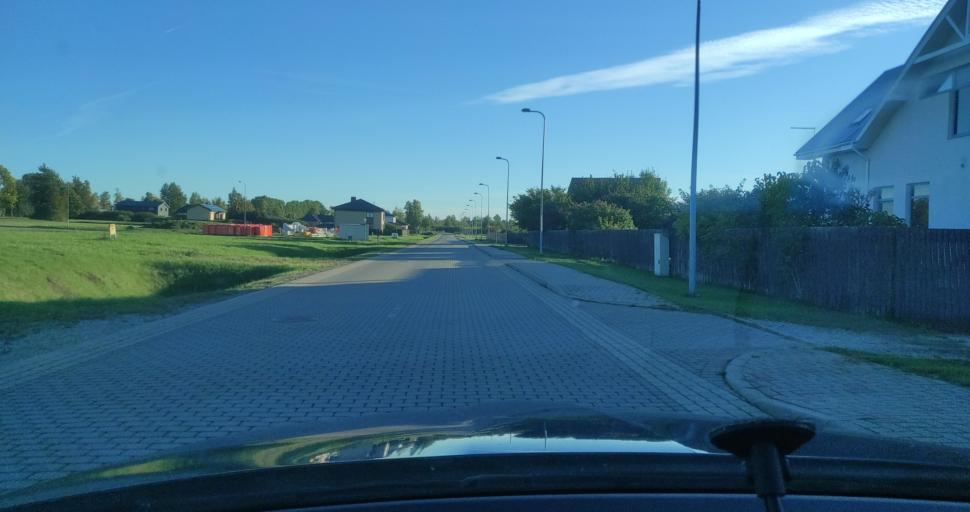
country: LV
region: Ventspils
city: Ventspils
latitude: 57.3684
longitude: 21.5746
